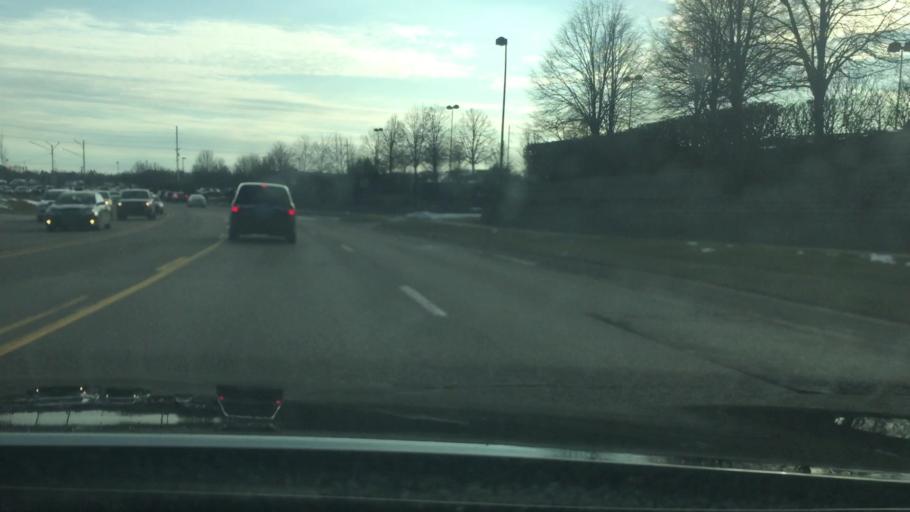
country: US
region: Michigan
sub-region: Wayne County
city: Northville
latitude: 42.4411
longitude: -83.4355
